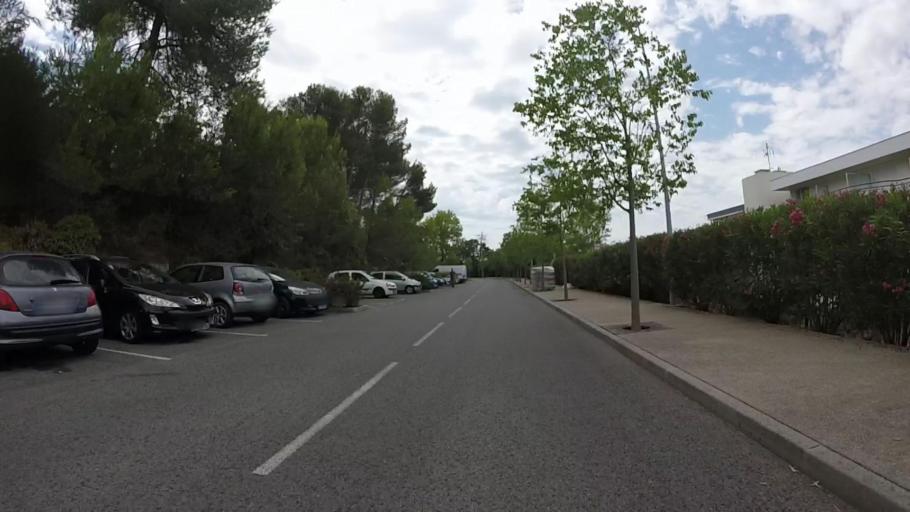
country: FR
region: Provence-Alpes-Cote d'Azur
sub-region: Departement des Alpes-Maritimes
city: Biot
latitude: 43.6181
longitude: 7.0765
